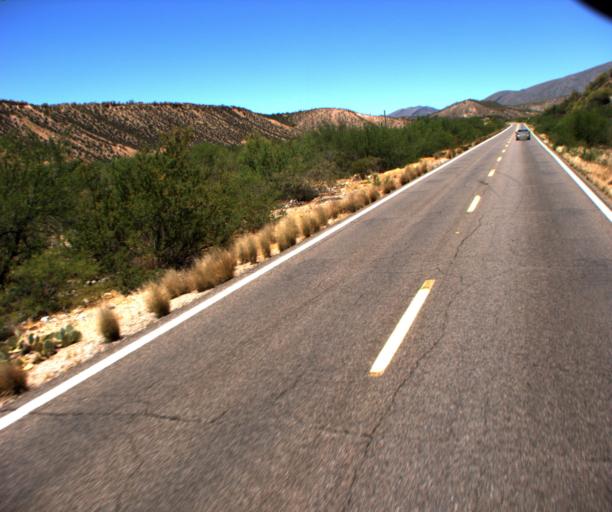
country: US
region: Arizona
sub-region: Pinal County
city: Kearny
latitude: 33.1200
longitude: -110.7726
